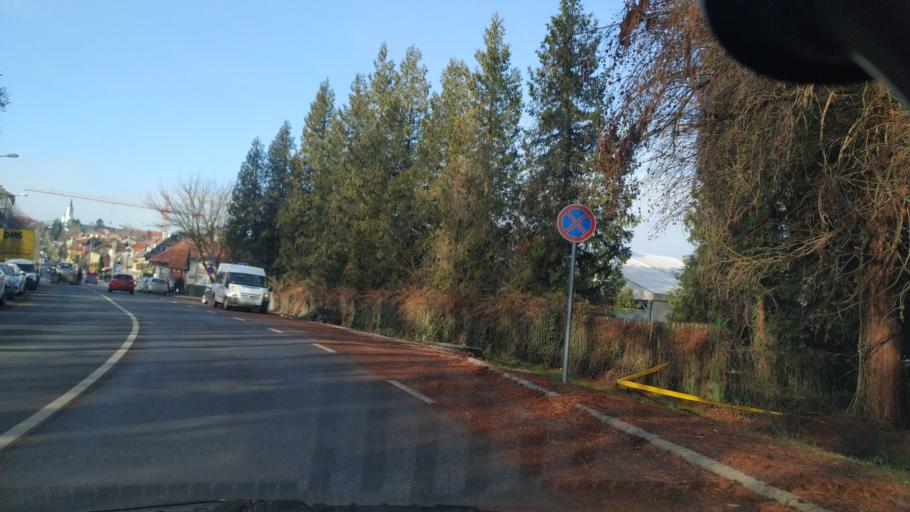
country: HU
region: Zala
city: Heviz
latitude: 46.7905
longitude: 17.1933
